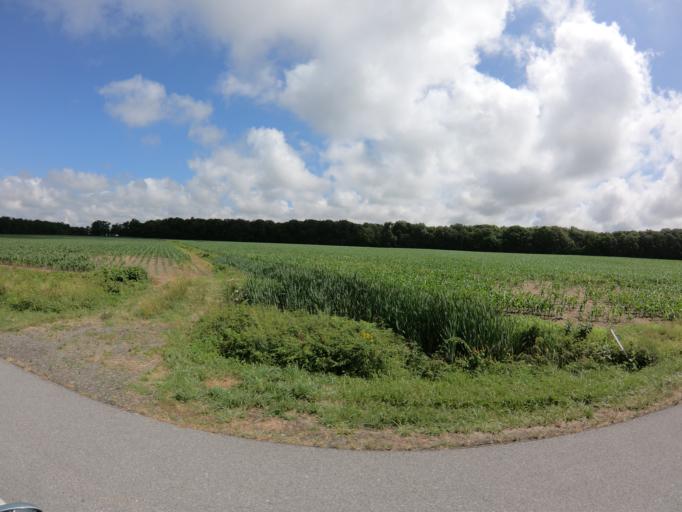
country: US
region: Maryland
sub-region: Caroline County
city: Ridgely
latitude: 39.1093
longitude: -75.9027
